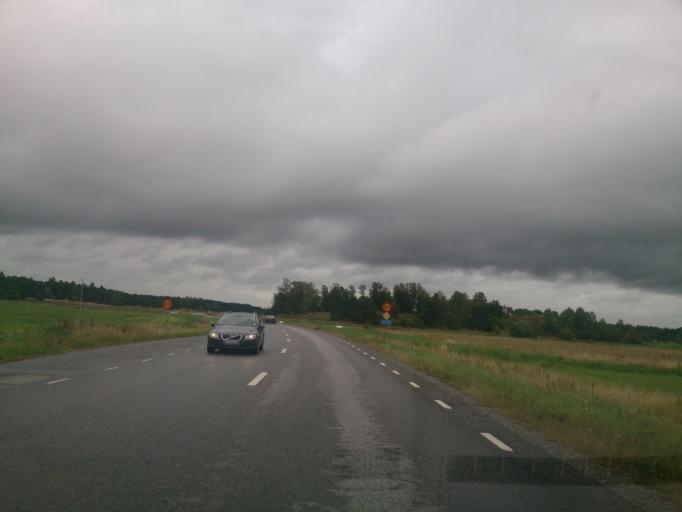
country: SE
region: OEstergoetland
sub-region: Norrkopings Kommun
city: Krokek
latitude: 58.5775
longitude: 16.5707
